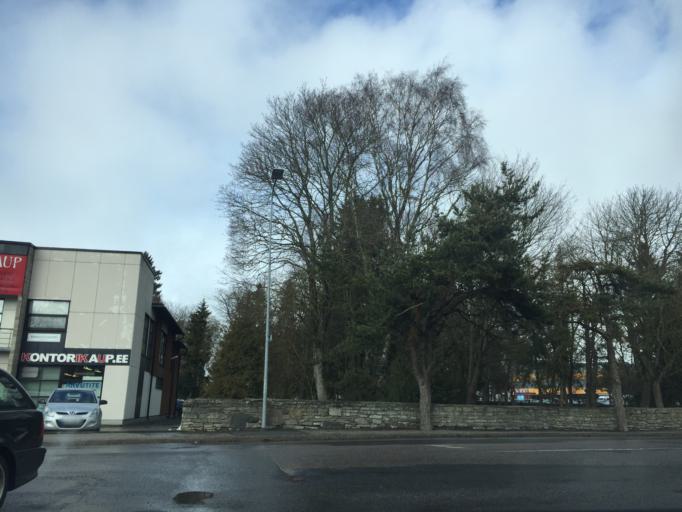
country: EE
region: Laeaene
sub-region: Haapsalu linn
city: Haapsalu
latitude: 58.9392
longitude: 23.5400
